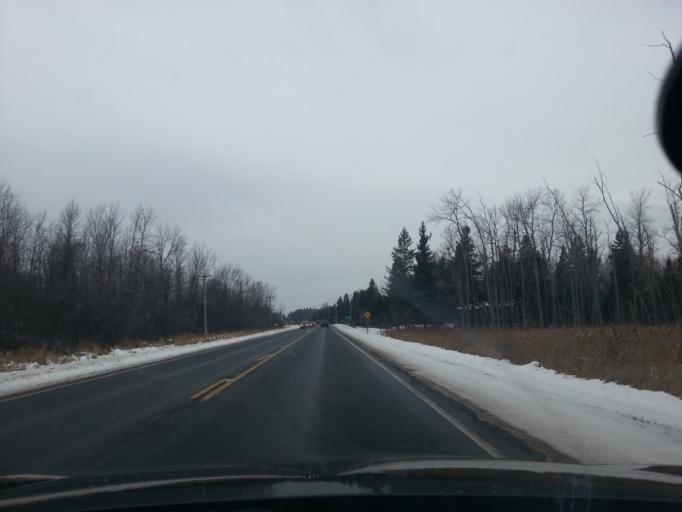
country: CA
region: Ontario
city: Carleton Place
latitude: 45.2947
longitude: -76.0864
